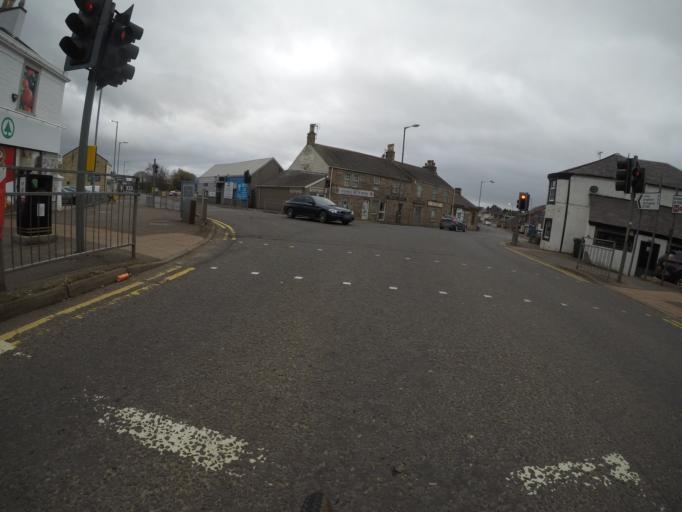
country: GB
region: Scotland
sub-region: East Ayrshire
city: Crosshouse
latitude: 55.6123
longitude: -4.5524
